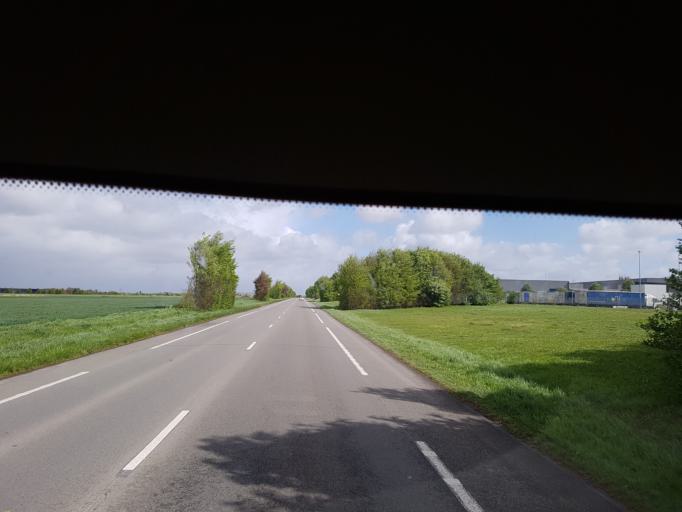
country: FR
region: Nord-Pas-de-Calais
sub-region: Departement du Nord
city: Raillencourt-Sainte-Olle
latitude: 50.1903
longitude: 3.1898
